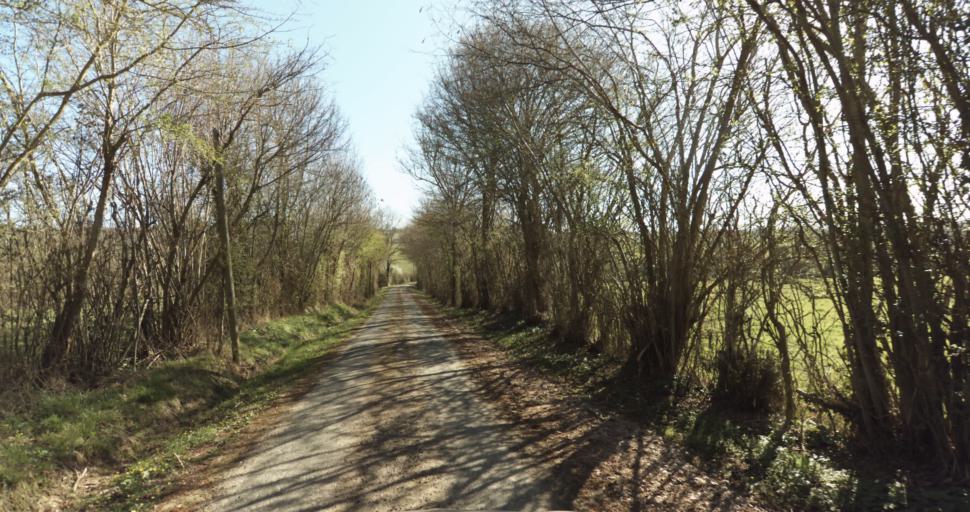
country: FR
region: Lower Normandy
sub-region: Departement de l'Orne
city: Trun
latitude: 48.9312
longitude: 0.0407
